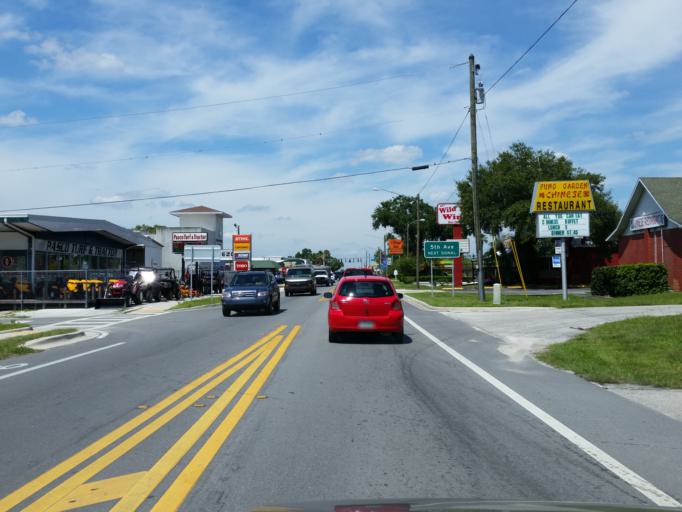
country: US
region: Florida
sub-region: Pasco County
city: Zephyrhills
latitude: 28.2315
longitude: -82.1805
